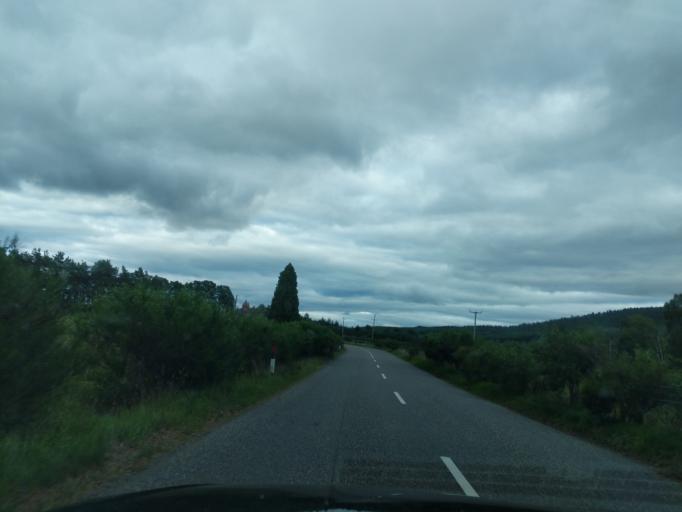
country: GB
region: Scotland
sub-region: Aberdeenshire
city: Aboyne
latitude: 57.0720
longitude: -2.8756
